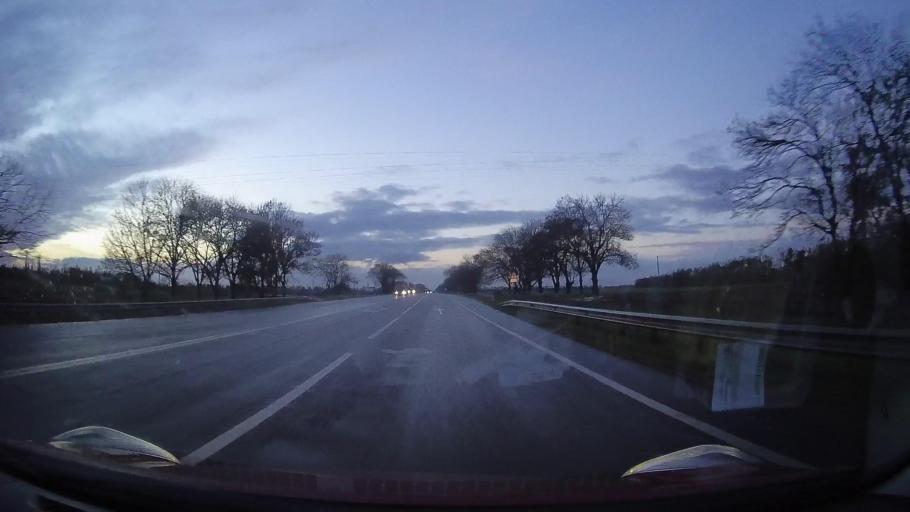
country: RU
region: Krasnodarskiy
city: Zavetnyy
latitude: 44.8824
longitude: 41.2249
